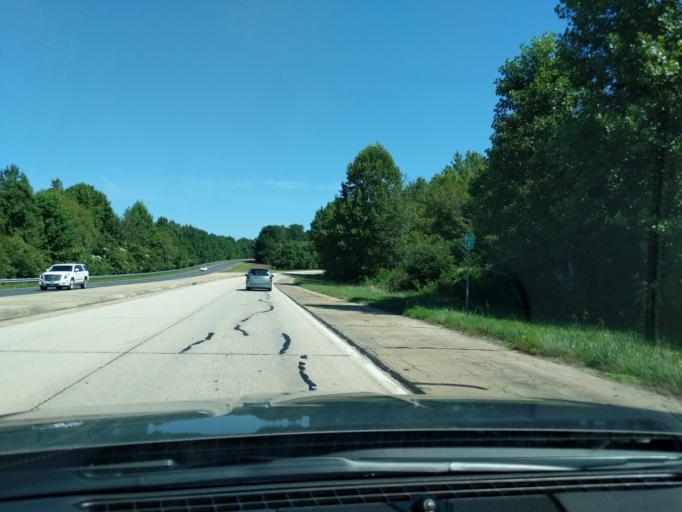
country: US
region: Georgia
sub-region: Habersham County
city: Cornelia
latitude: 34.5155
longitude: -83.5449
